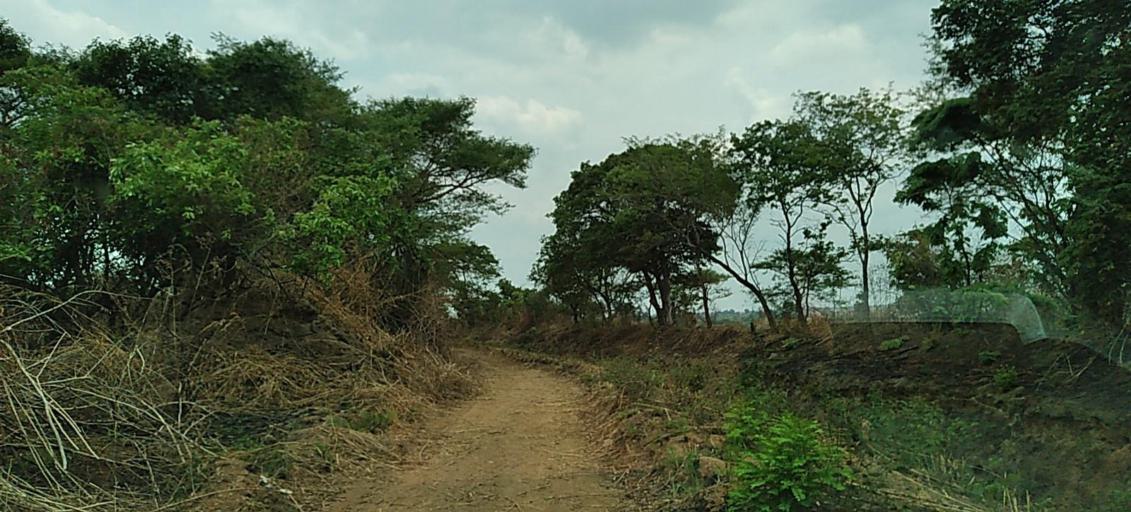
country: ZM
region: Copperbelt
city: Chililabombwe
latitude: -12.3600
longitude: 27.8023
